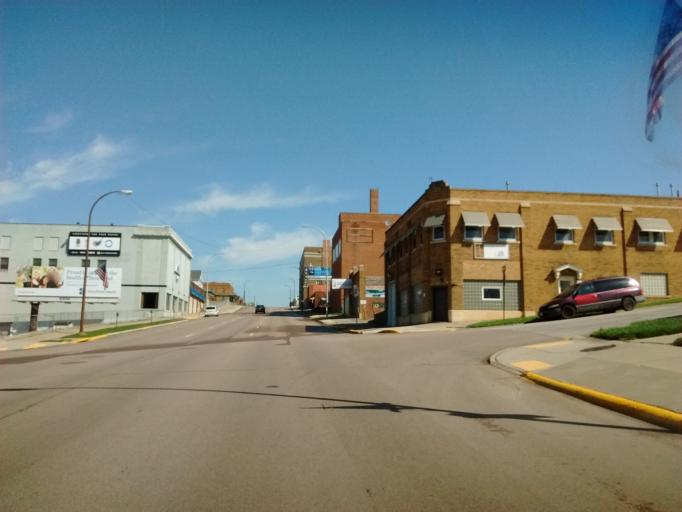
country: US
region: Iowa
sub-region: Woodbury County
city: Sioux City
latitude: 42.4972
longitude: -96.4034
